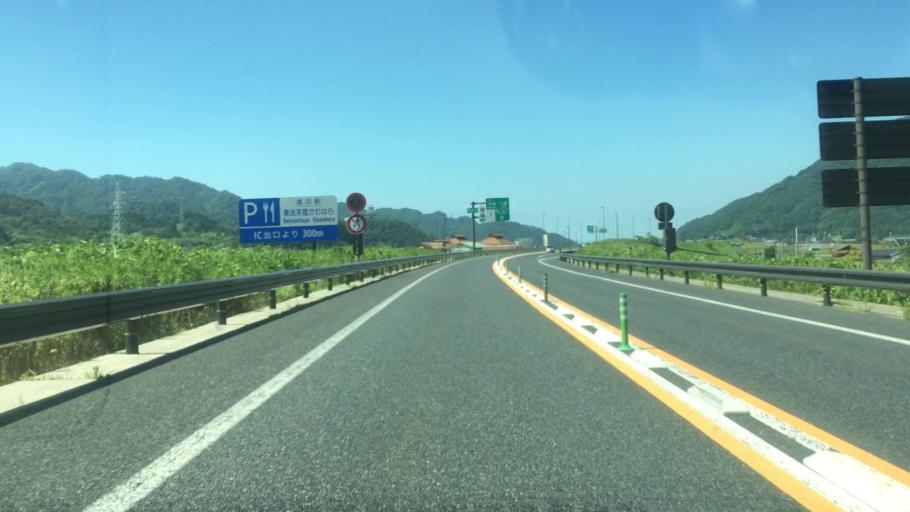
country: JP
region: Tottori
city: Tottori
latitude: 35.3896
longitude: 134.2034
